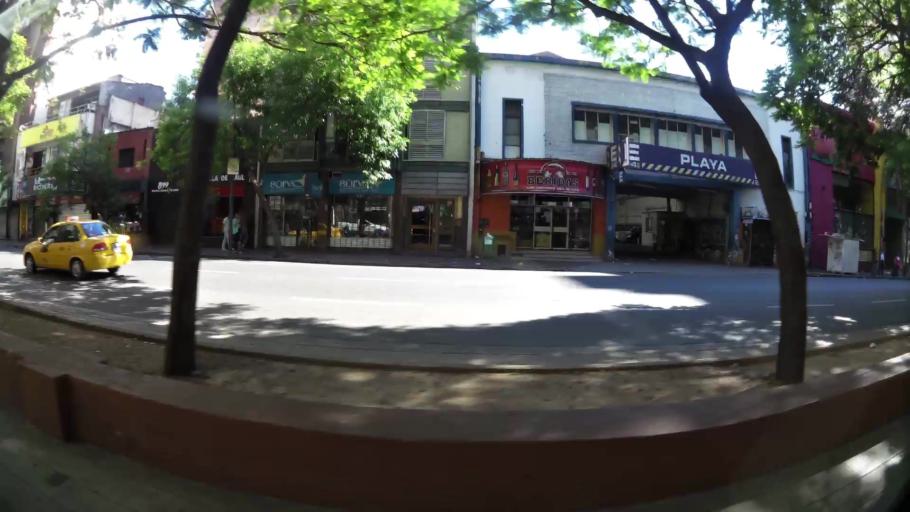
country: AR
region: Cordoba
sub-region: Departamento de Capital
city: Cordoba
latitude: -31.4206
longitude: -64.1868
